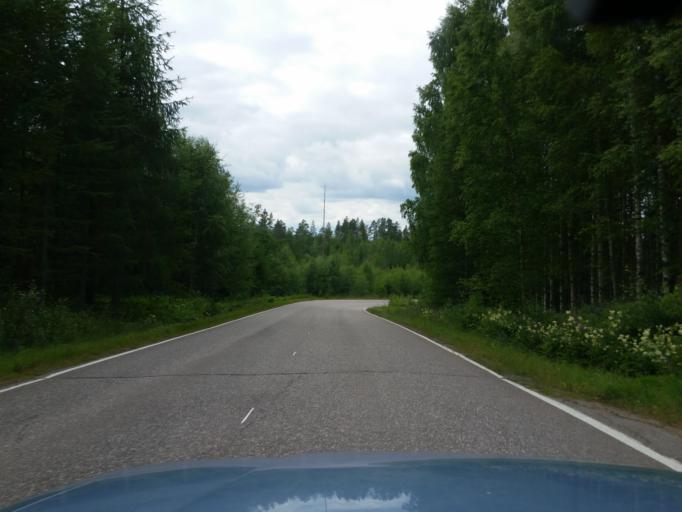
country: FI
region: Southern Savonia
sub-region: Savonlinna
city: Sulkava
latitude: 61.7935
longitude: 28.4044
